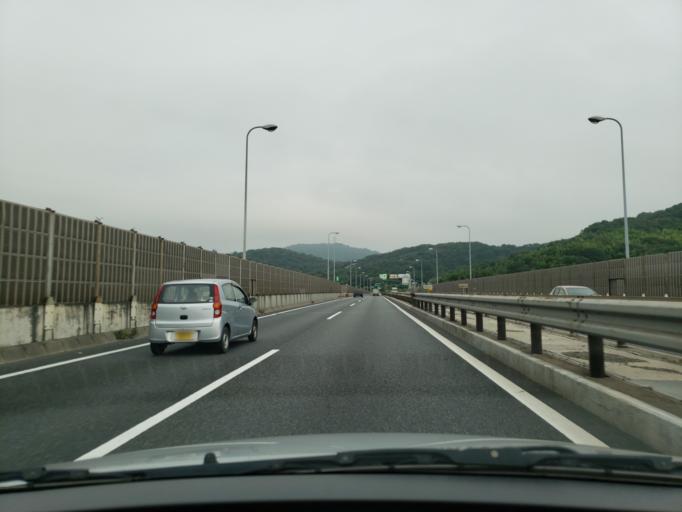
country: JP
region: Hyogo
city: Himeji
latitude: 34.8166
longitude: 134.6511
